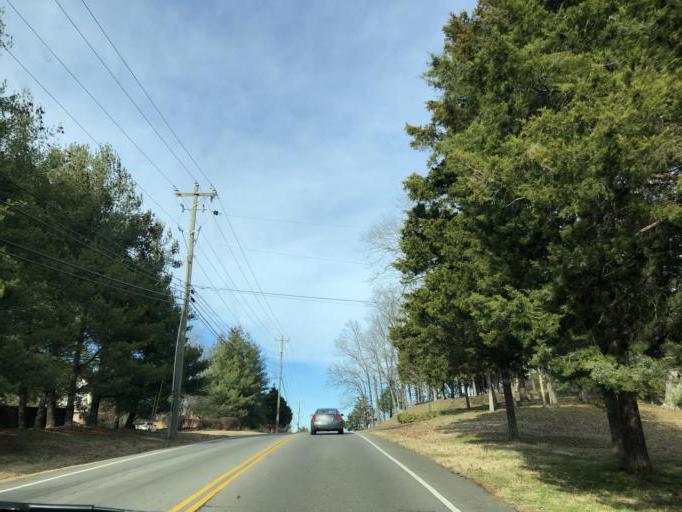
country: US
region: Tennessee
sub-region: Wilson County
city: Green Hill
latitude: 36.1576
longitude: -86.5860
